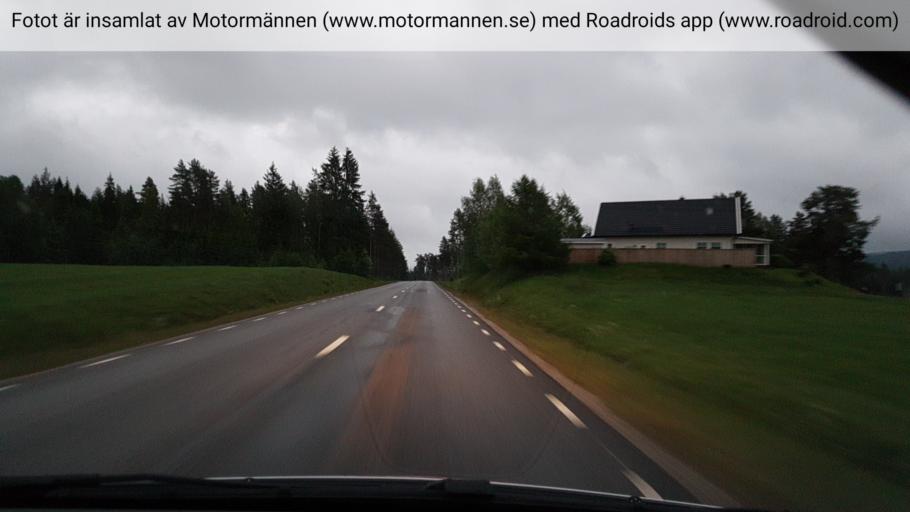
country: SE
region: Vaestmanland
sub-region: Skinnskattebergs Kommun
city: Skinnskatteberg
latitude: 59.9108
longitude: 15.4839
